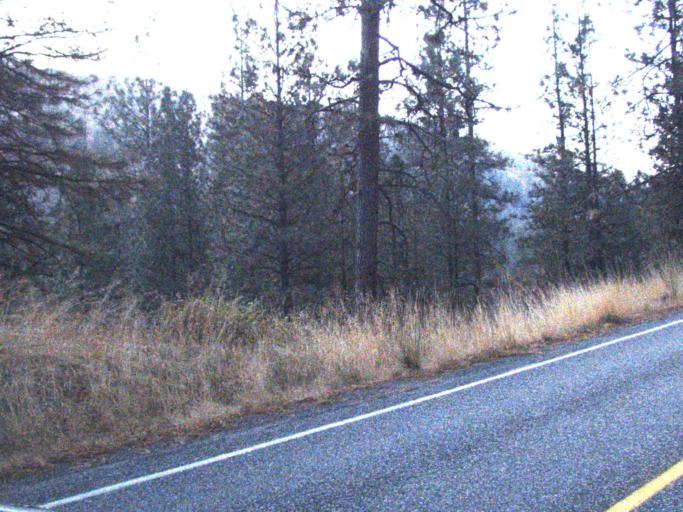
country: US
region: Washington
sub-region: Okanogan County
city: Coulee Dam
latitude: 48.1373
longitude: -118.6938
